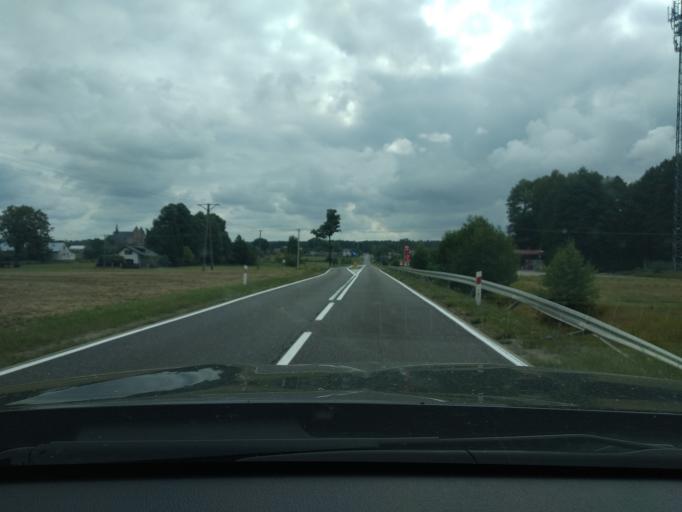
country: PL
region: Masovian Voivodeship
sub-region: Powiat pultuski
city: Obryte
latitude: 52.6508
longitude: 21.2423
